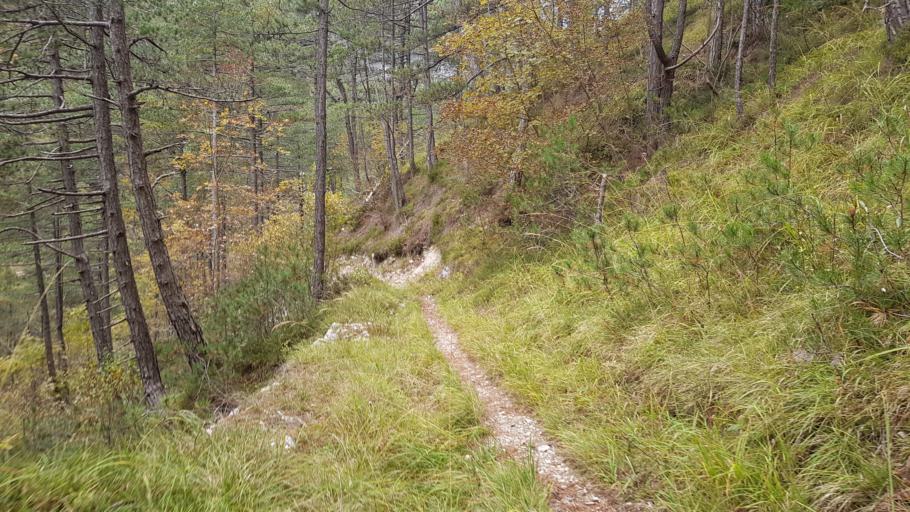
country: IT
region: Friuli Venezia Giulia
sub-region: Provincia di Udine
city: Chiusaforte
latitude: 46.4163
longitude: 13.3295
